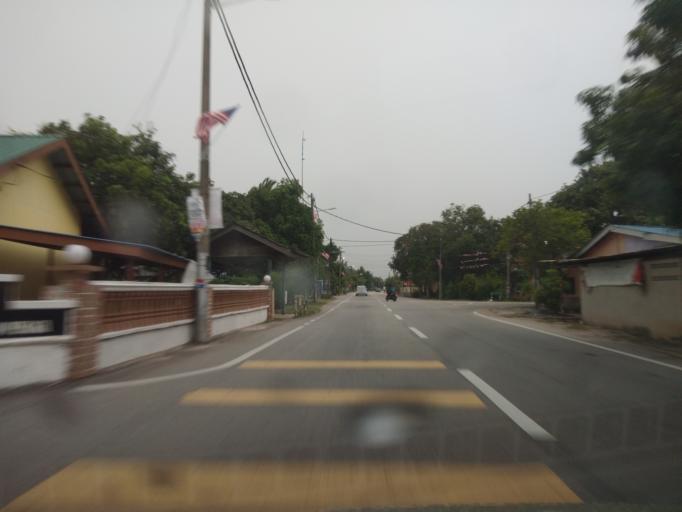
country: MY
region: Penang
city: Permatang Kuching
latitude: 5.4900
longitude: 100.3996
